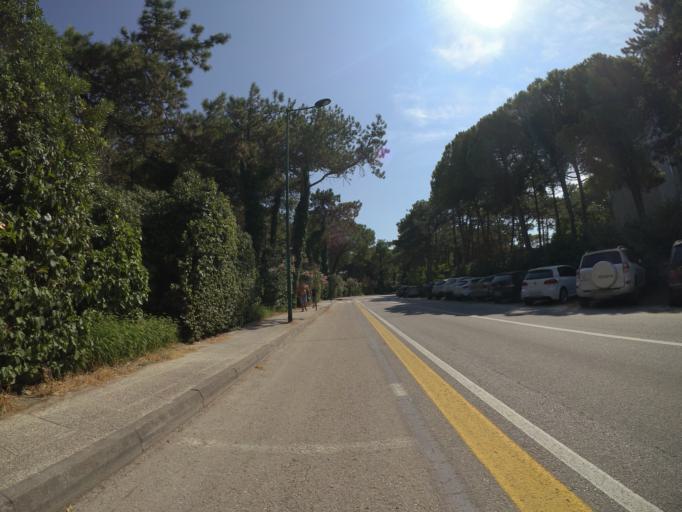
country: IT
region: Friuli Venezia Giulia
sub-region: Provincia di Udine
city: Lignano Sabbiadoro
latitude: 45.6528
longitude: 13.1017
